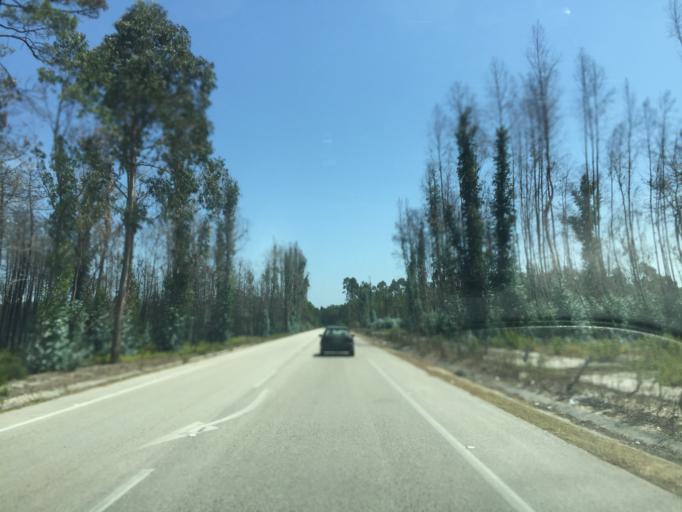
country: PT
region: Coimbra
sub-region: Mira
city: Mira
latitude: 40.3365
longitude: -8.7478
